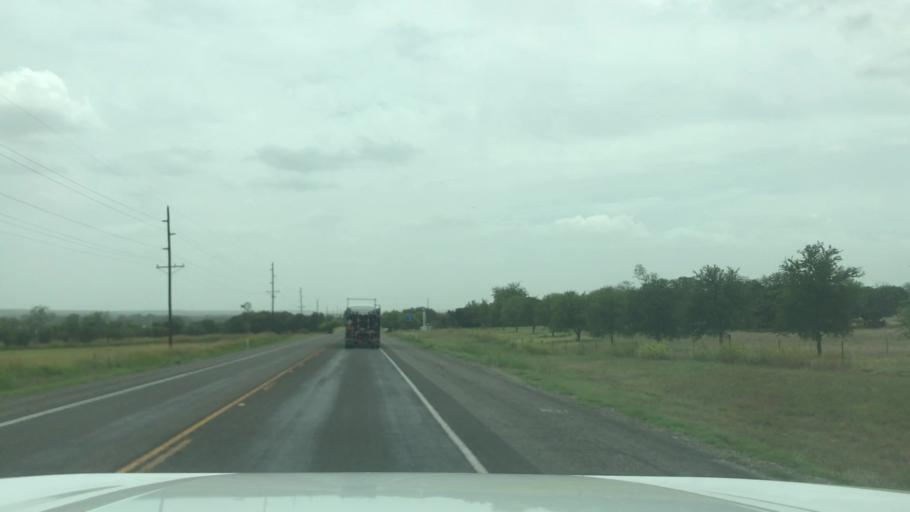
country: US
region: Texas
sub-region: Bosque County
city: Clifton
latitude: 31.7557
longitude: -97.5599
